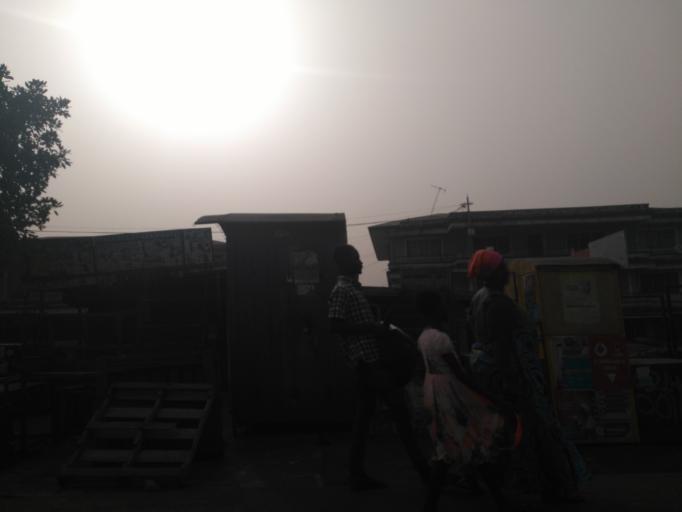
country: GH
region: Ashanti
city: Tafo
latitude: 6.7216
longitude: -1.6333
